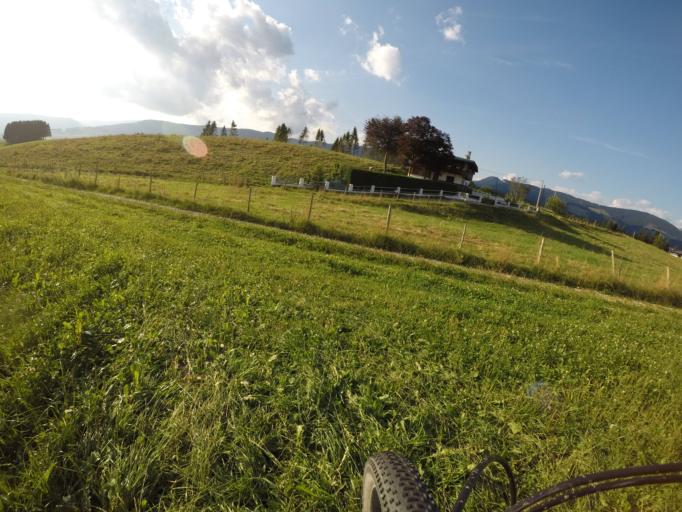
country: IT
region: Veneto
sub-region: Provincia di Vicenza
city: Gallio
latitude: 45.8766
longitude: 11.5255
